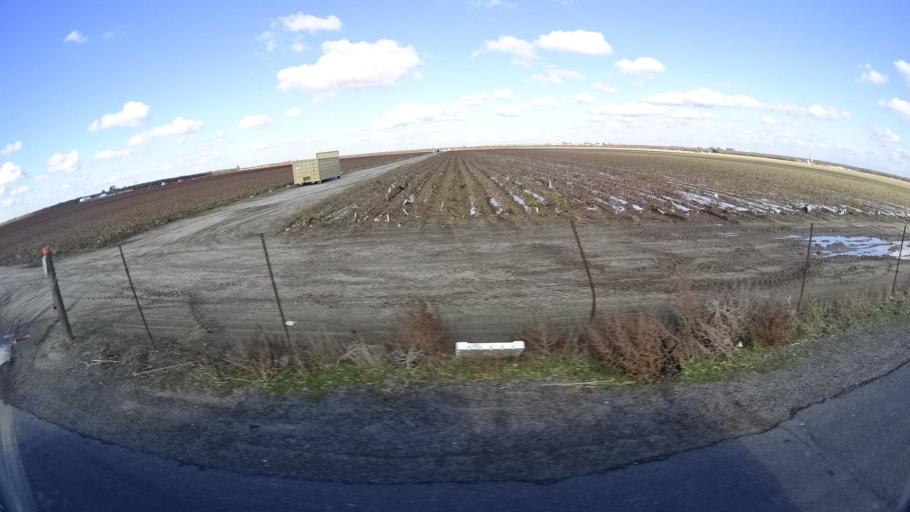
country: US
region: California
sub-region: Kern County
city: McFarland
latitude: 35.7178
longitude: -119.2537
